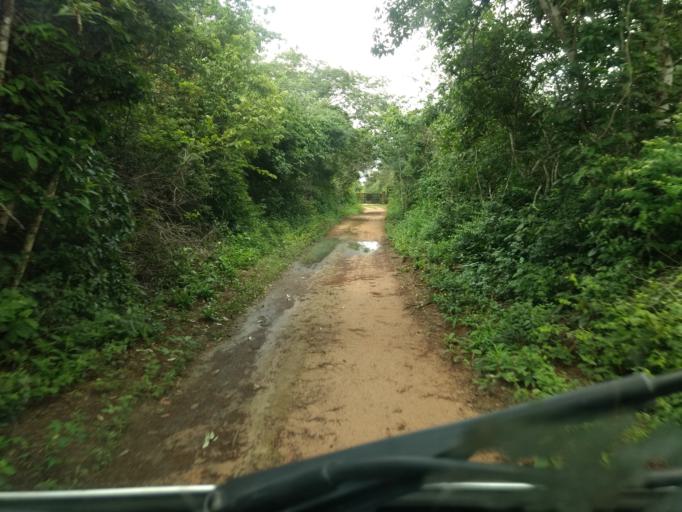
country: BR
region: Ceara
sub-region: Crateus
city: Crateus
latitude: -5.1810
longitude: -40.9398
